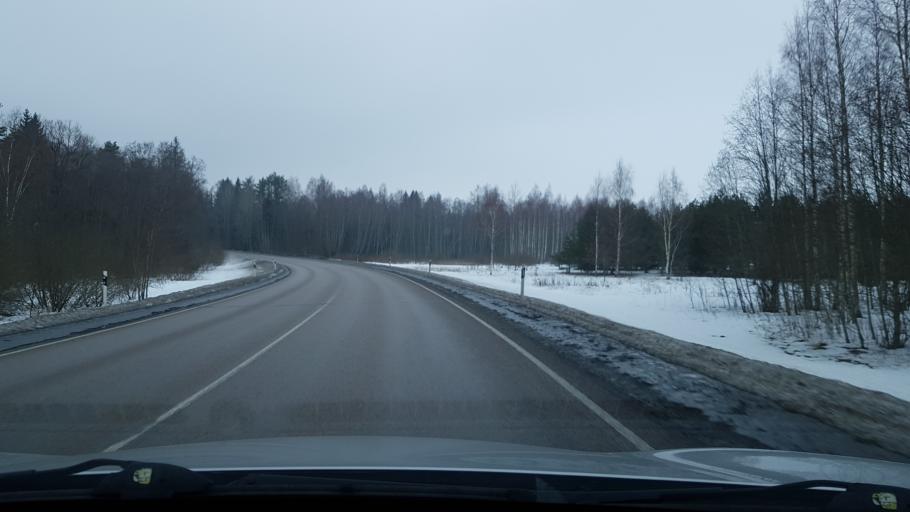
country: EE
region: Valgamaa
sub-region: Torva linn
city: Torva
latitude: 57.9963
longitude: 26.1709
